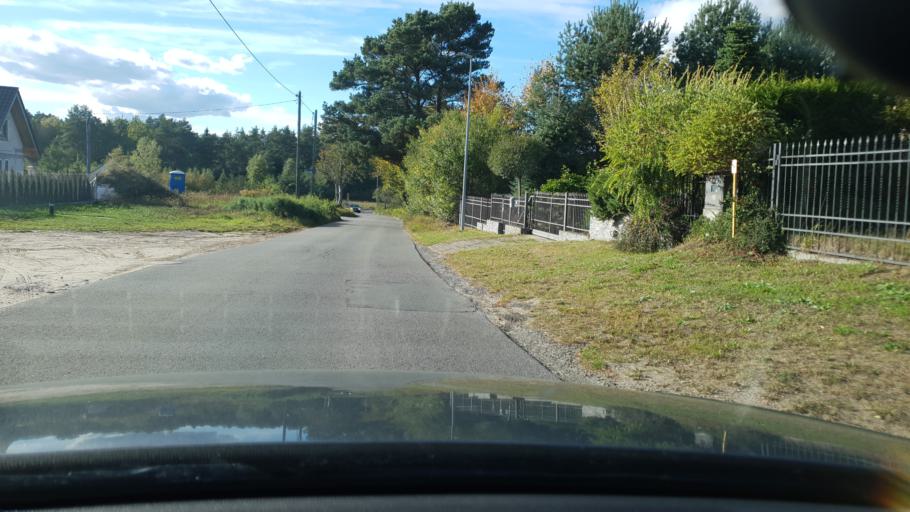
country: PL
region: Pomeranian Voivodeship
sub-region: Powiat kartuski
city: Chwaszczyno
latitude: 54.4818
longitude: 18.4292
